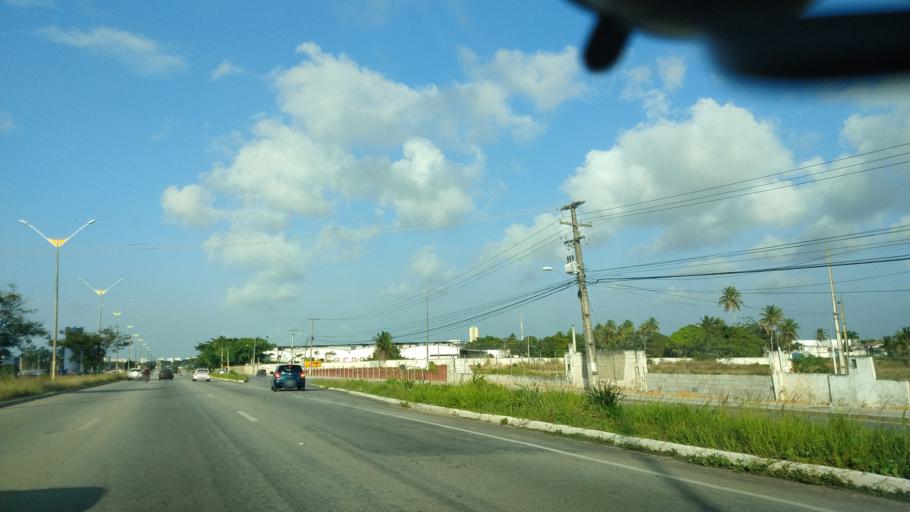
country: BR
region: Rio Grande do Norte
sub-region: Parnamirim
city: Parnamirim
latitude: -5.8887
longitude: -35.2413
